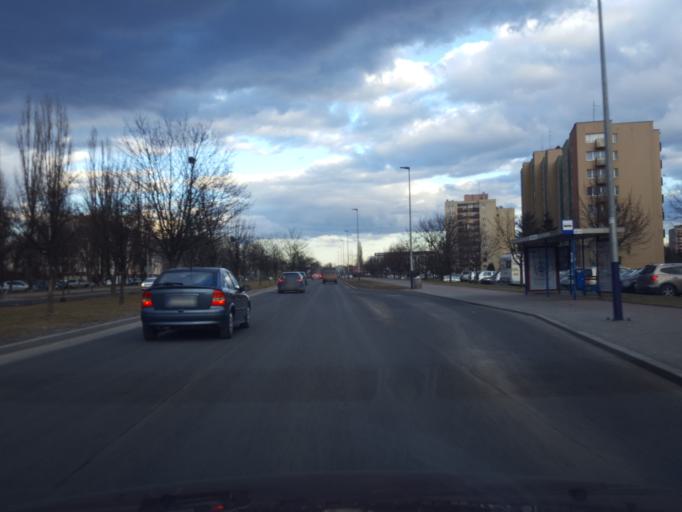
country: PL
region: Lesser Poland Voivodeship
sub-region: Krakow
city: Krakow
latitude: 50.0761
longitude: 20.0069
